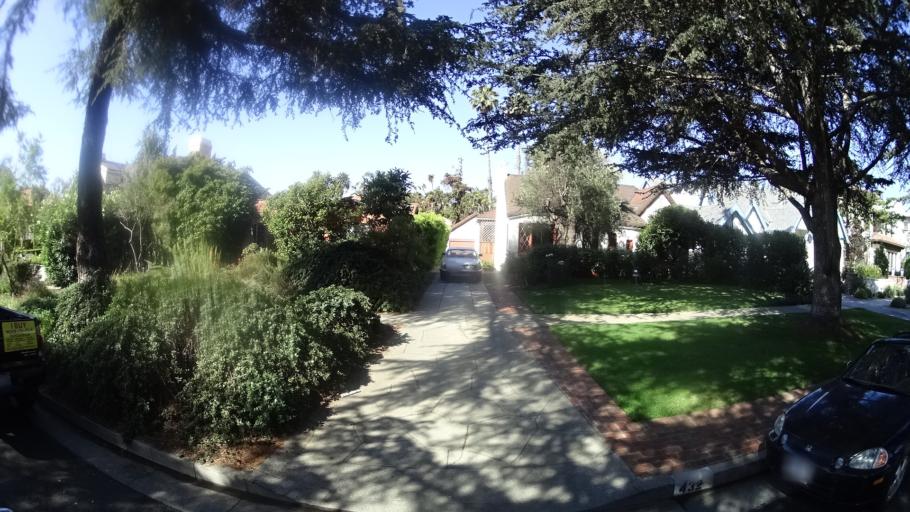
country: US
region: California
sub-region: Los Angeles County
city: Santa Monica
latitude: 34.0373
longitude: -118.4975
